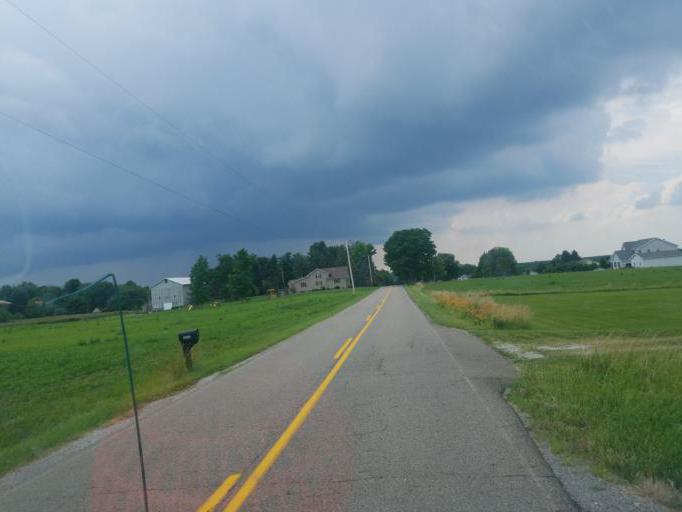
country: US
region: Ohio
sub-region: Mahoning County
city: Sebring
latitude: 40.9741
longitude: -80.9412
